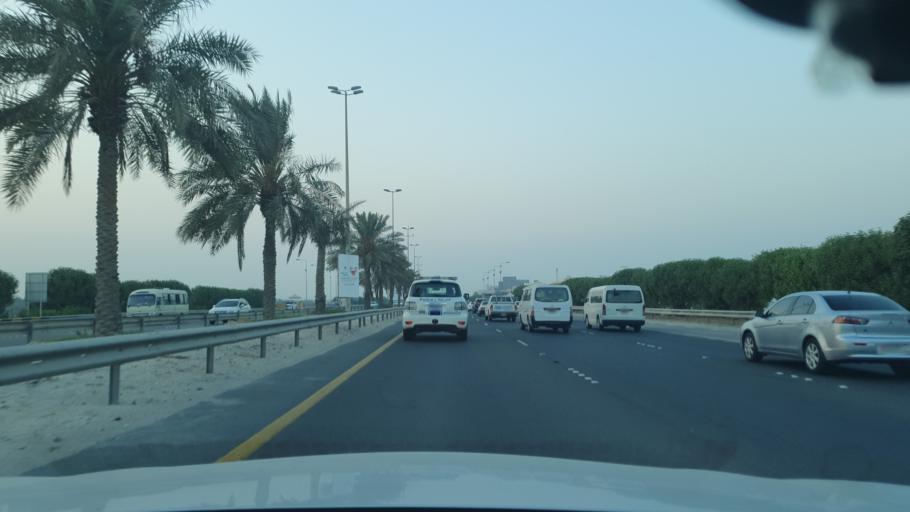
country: BH
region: Central Governorate
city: Madinat Hamad
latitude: 26.1495
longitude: 50.5081
